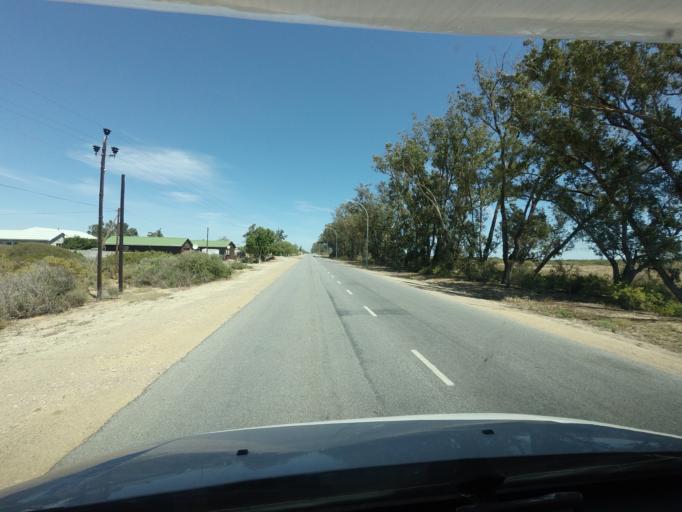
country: ZA
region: Western Cape
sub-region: West Coast District Municipality
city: Vredenburg
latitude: -32.7875
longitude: 18.1985
